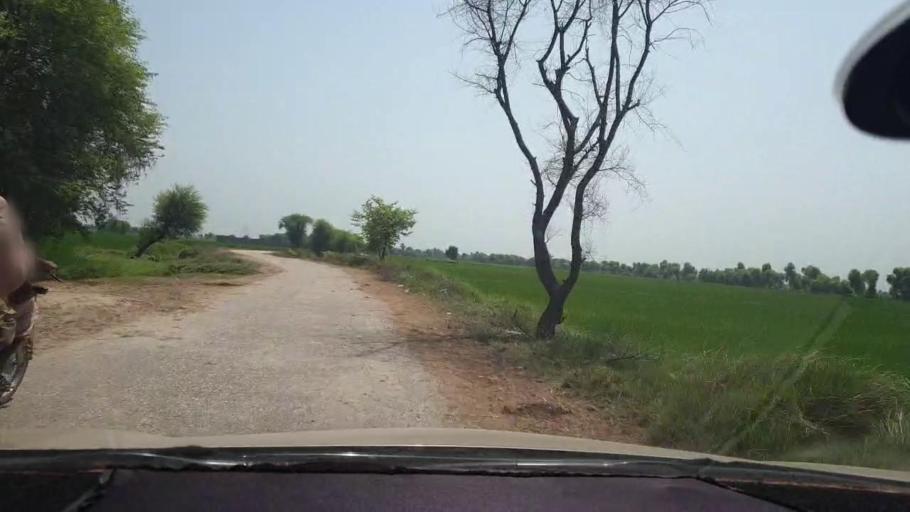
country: PK
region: Sindh
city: Kambar
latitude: 27.6816
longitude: 67.9390
